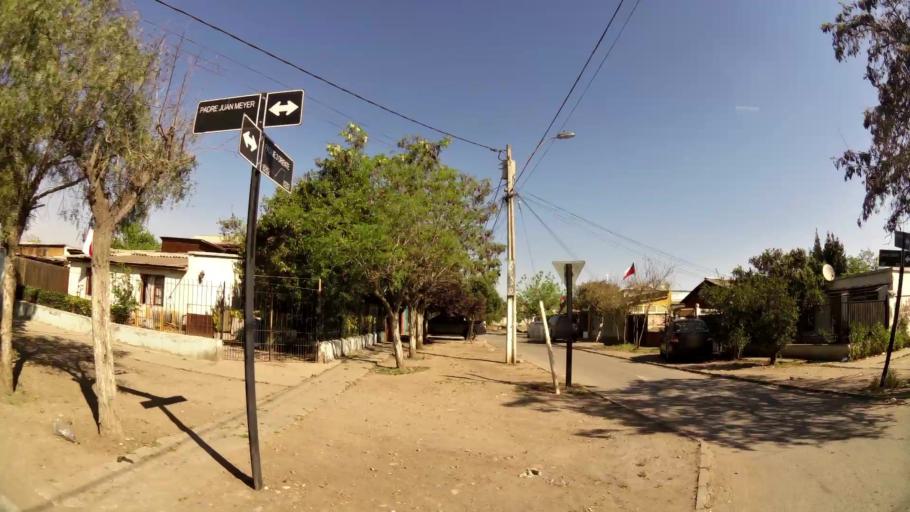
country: CL
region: Santiago Metropolitan
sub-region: Provincia de Santiago
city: La Pintana
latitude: -33.5354
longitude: -70.6181
